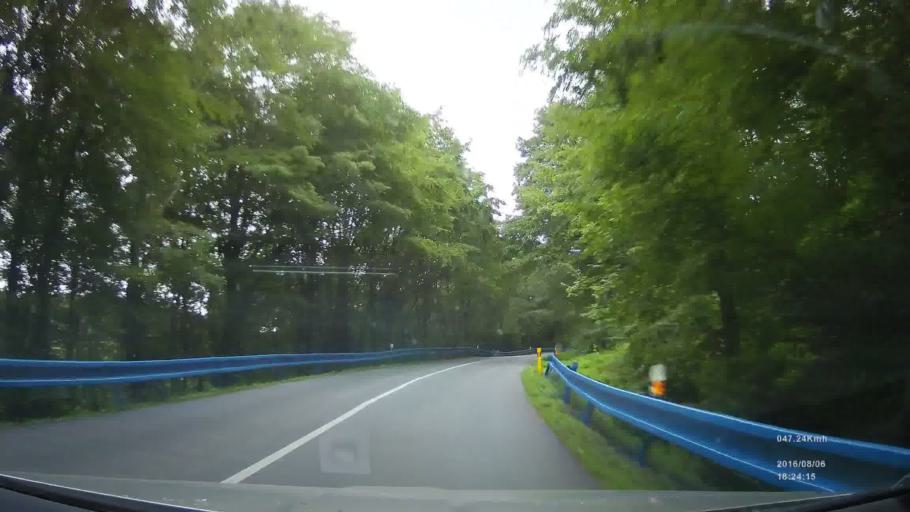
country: SK
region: Presovsky
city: Svidnik
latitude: 49.2967
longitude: 21.5697
